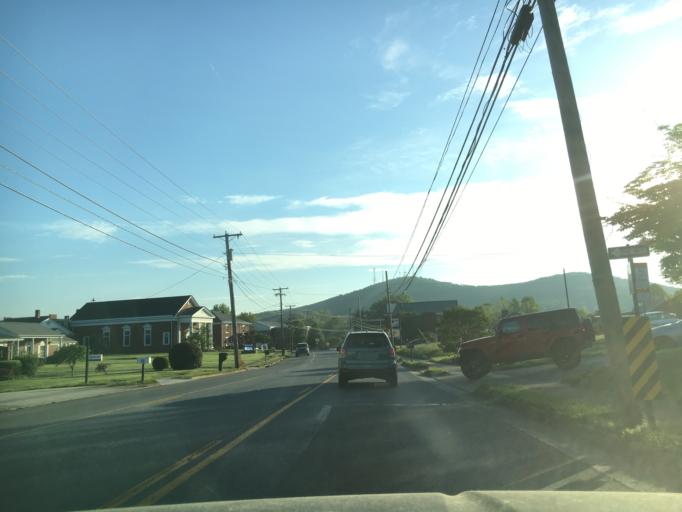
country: US
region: Virginia
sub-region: Campbell County
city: Rustburg
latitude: 37.2748
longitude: -79.1039
